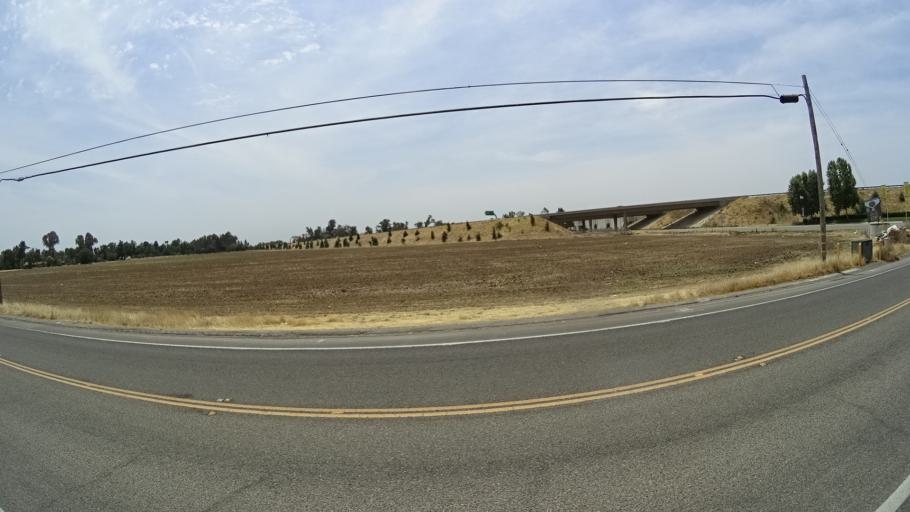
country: US
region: California
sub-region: Fresno County
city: Sunnyside
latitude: 36.7506
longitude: -119.6724
